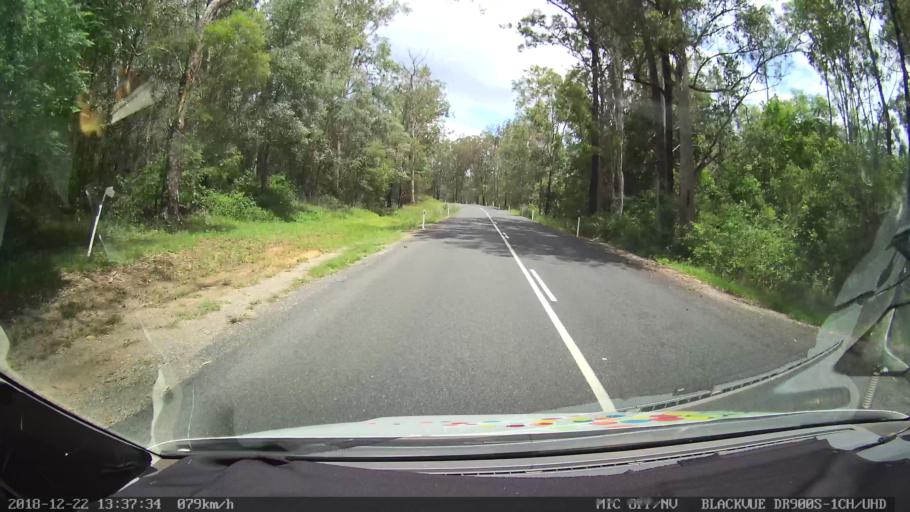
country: AU
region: New South Wales
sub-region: Clarence Valley
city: Coutts Crossing
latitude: -29.8914
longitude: 152.7881
